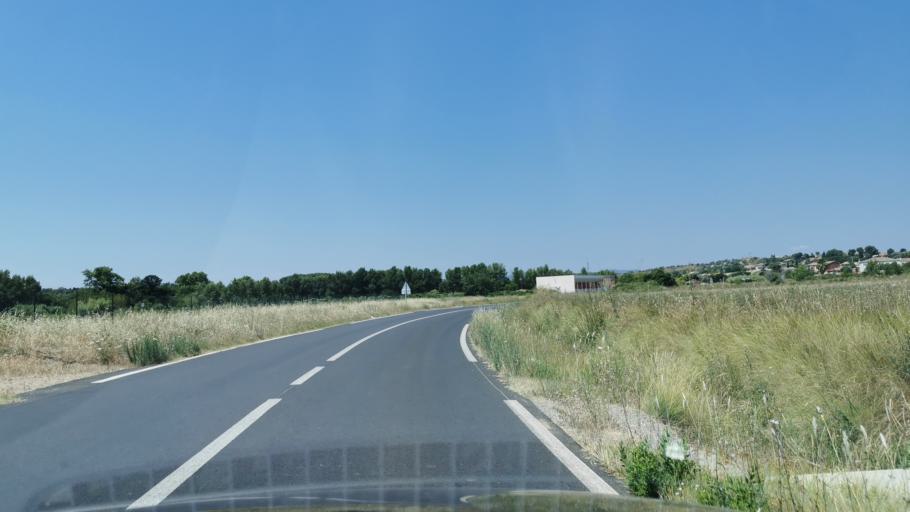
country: FR
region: Languedoc-Roussillon
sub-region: Departement de l'Herault
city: Cazouls-les-Beziers
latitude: 43.3815
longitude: 3.1060
